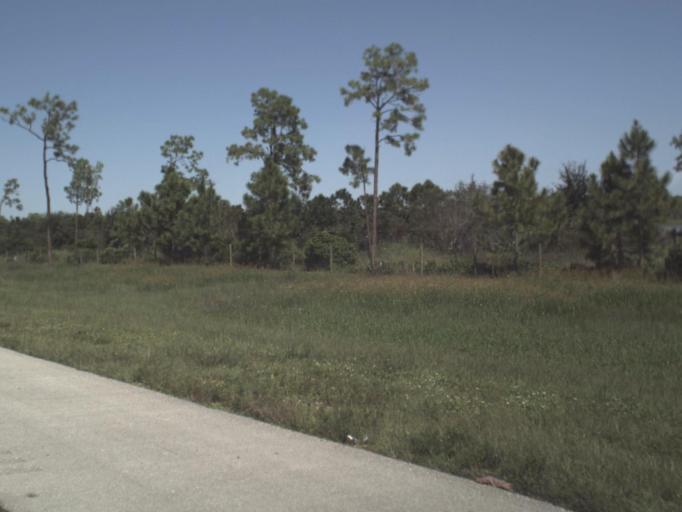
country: US
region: Florida
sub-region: Lee County
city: Bonita Springs
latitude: 26.3782
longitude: -81.7719
